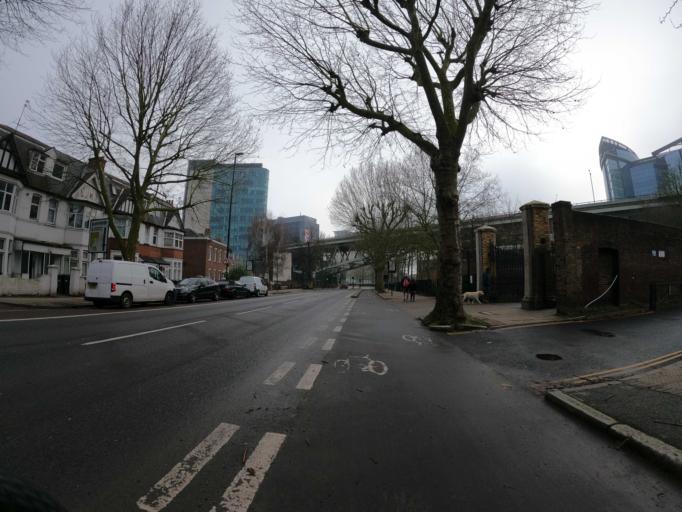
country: GB
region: England
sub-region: Greater London
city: Brentford
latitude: 51.4901
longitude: -0.3157
